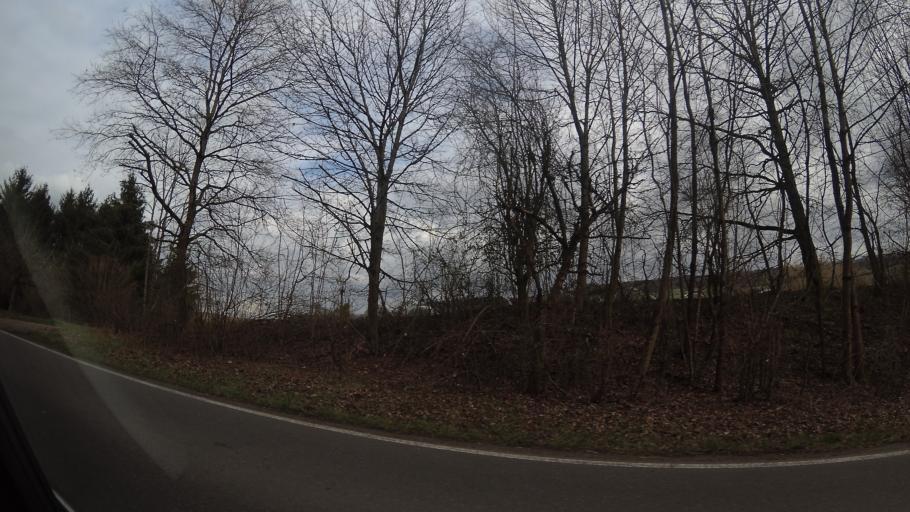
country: DE
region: Saarland
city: Gersheim
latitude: 49.1784
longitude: 7.2361
